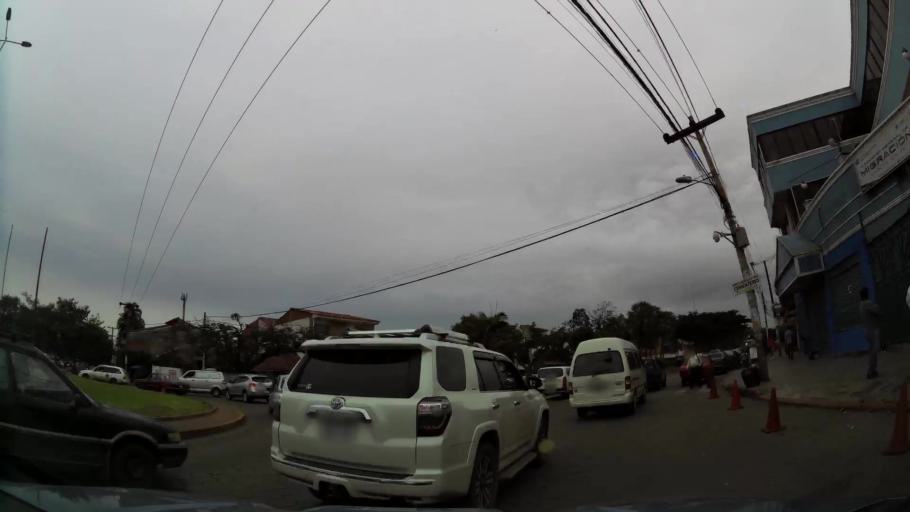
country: BO
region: Santa Cruz
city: Santa Cruz de la Sierra
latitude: -17.7982
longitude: -63.1864
